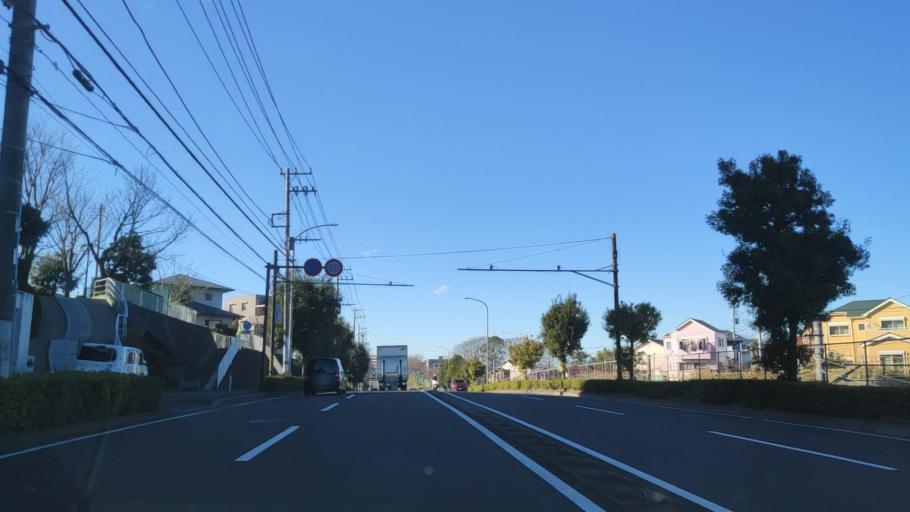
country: JP
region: Tokyo
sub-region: Machida-shi
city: Machida
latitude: 35.5209
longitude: 139.5270
